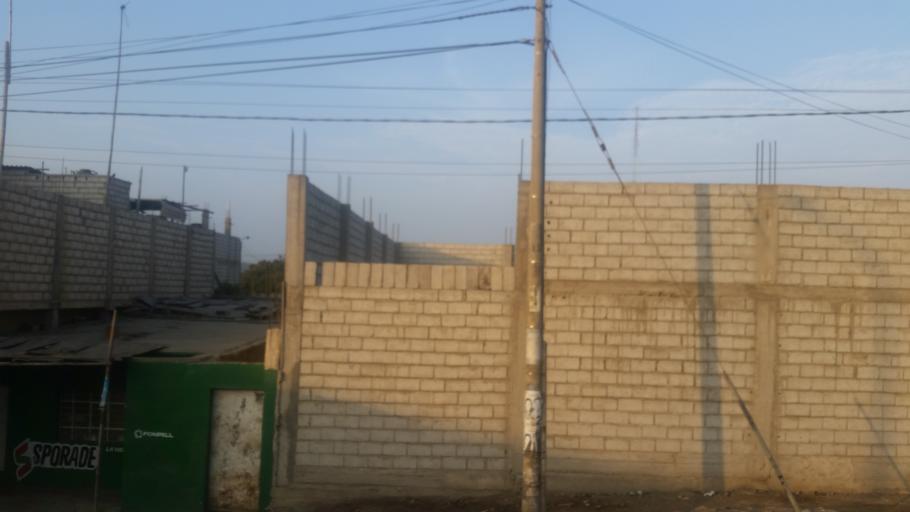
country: PE
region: La Libertad
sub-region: Ascope
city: Chocope
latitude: -7.7923
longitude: -79.2246
